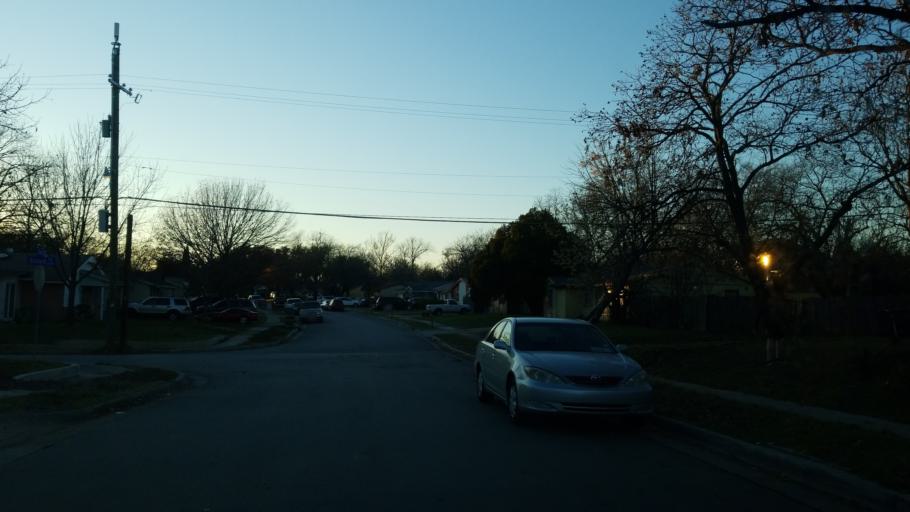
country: US
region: Texas
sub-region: Tarrant County
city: Arlington
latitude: 32.7322
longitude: -97.0578
